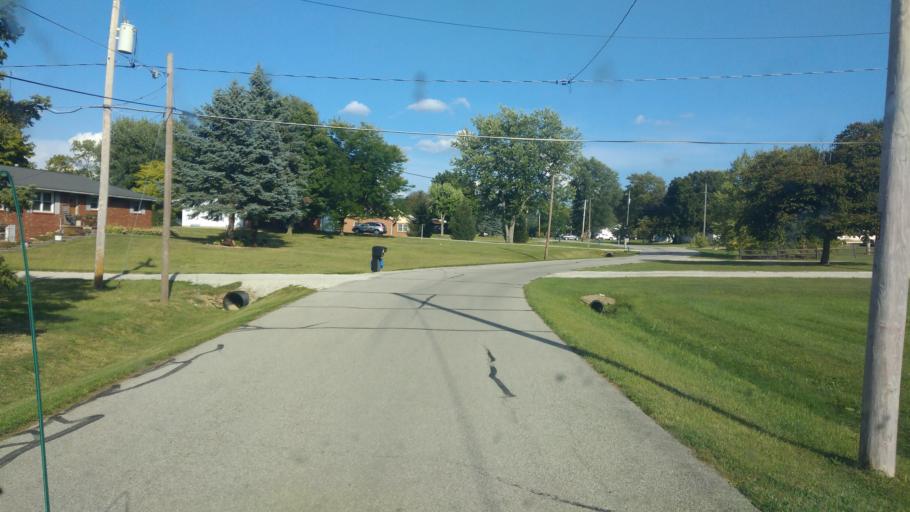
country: US
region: Ohio
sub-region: Crawford County
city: Galion
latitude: 40.7575
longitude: -82.7822
